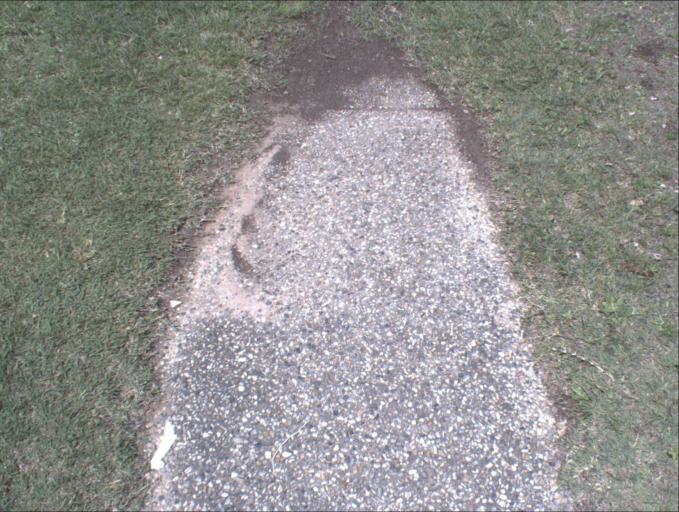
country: AU
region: Queensland
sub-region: Logan
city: North Maclean
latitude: -27.8126
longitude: 152.9552
